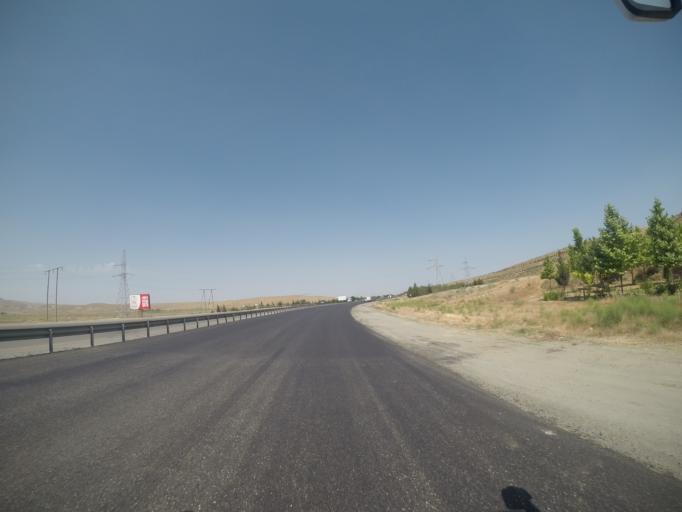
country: AZ
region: Haciqabul
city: Haciqabul
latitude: 40.0413
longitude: 48.9601
